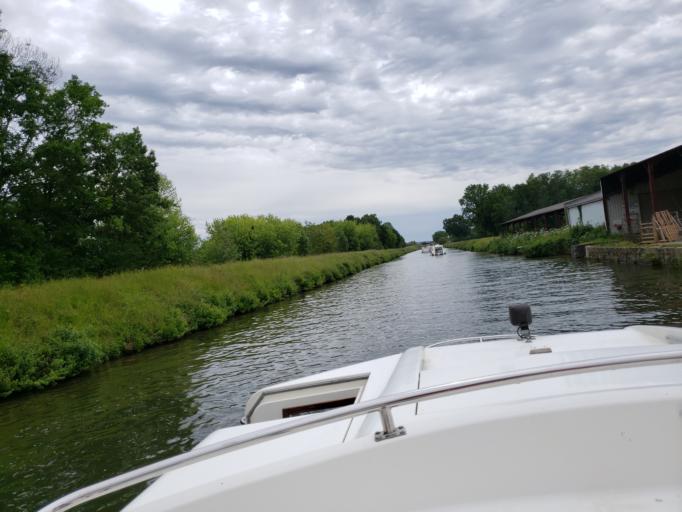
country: FR
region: Bourgogne
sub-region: Departement de l'Yonne
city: Appoigny
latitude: 47.8853
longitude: 3.5448
